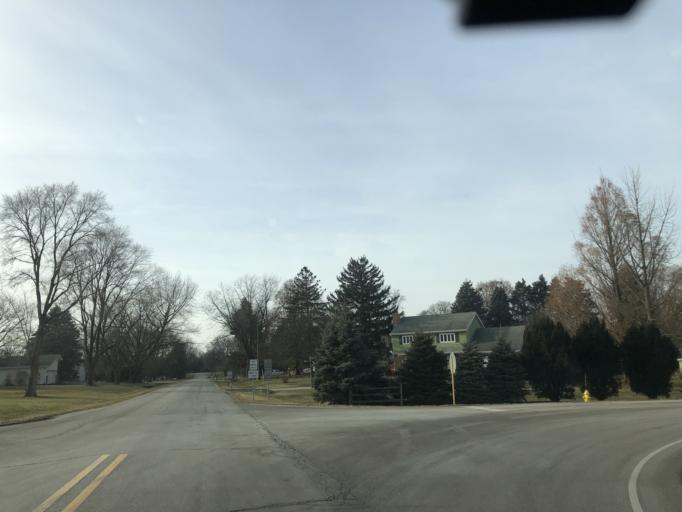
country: US
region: Illinois
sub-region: Cook County
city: Lemont
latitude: 41.7111
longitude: -88.0072
